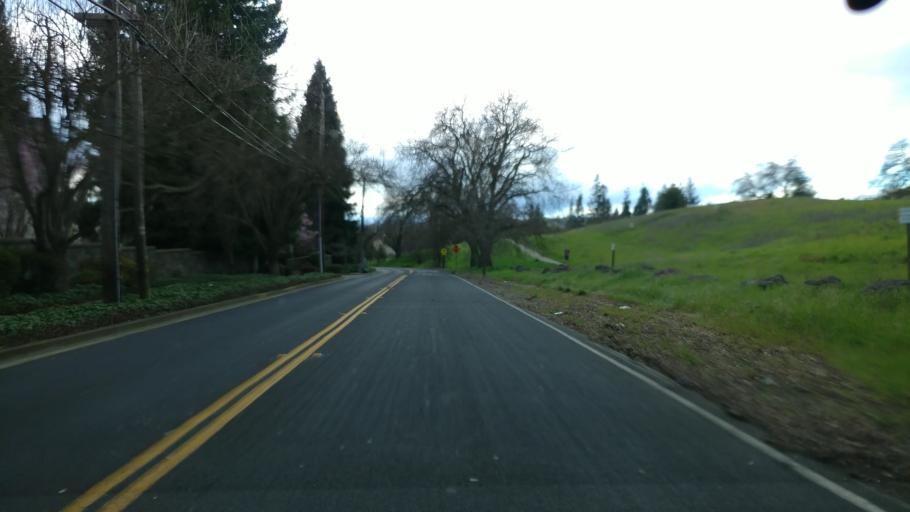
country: US
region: California
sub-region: Contra Costa County
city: Diablo
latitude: 37.8314
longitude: -121.9498
